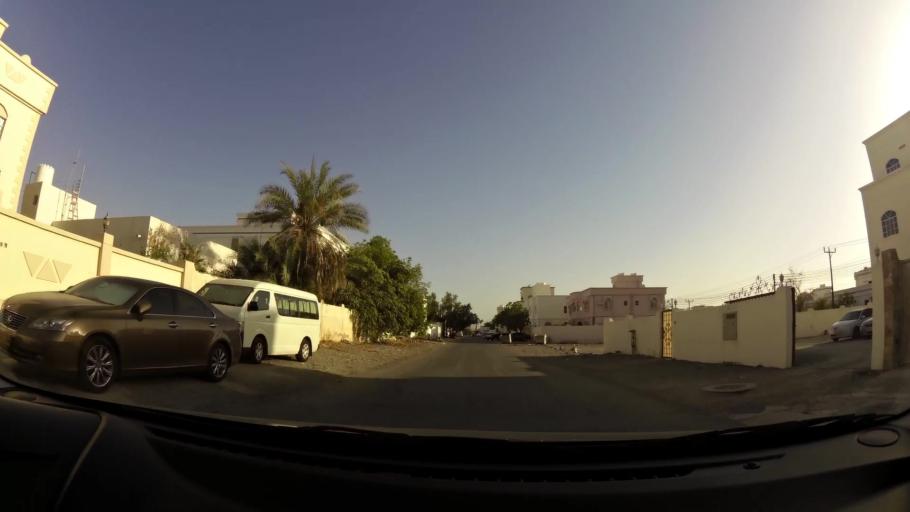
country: OM
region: Muhafazat Masqat
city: As Sib al Jadidah
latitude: 23.6342
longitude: 58.1943
